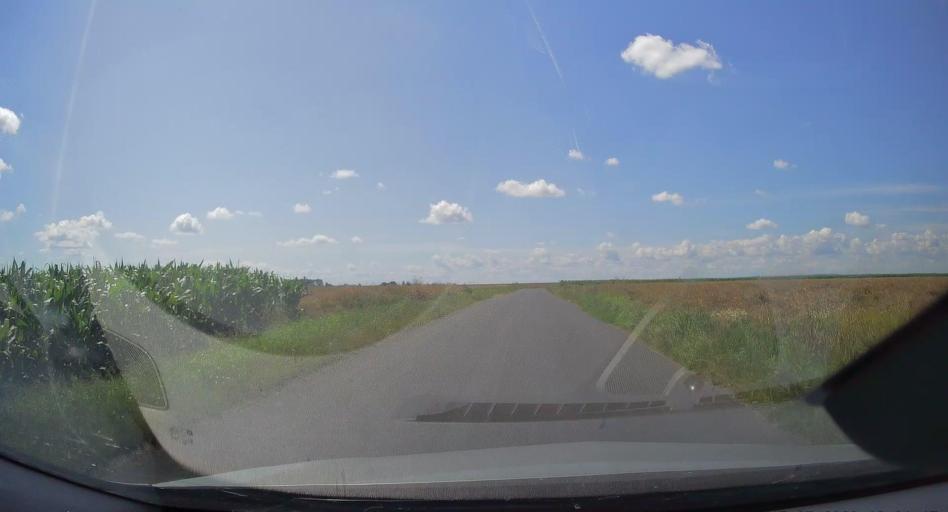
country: PL
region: Subcarpathian Voivodeship
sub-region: Powiat jaroslawski
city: Sosnica
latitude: 49.8515
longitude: 22.8779
